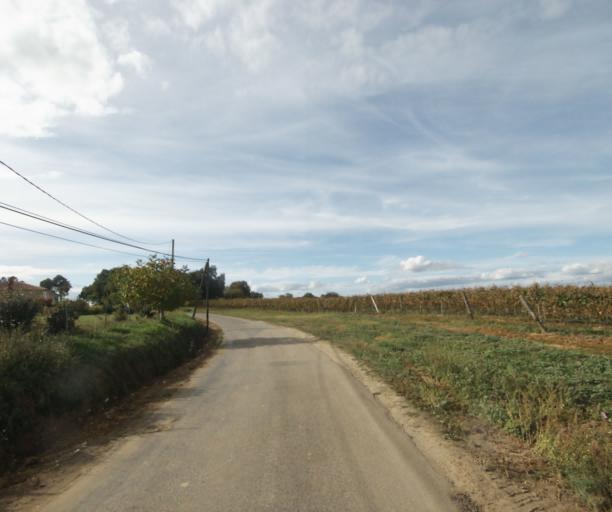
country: FR
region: Midi-Pyrenees
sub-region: Departement du Gers
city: Gondrin
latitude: 43.8745
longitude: 0.2416
